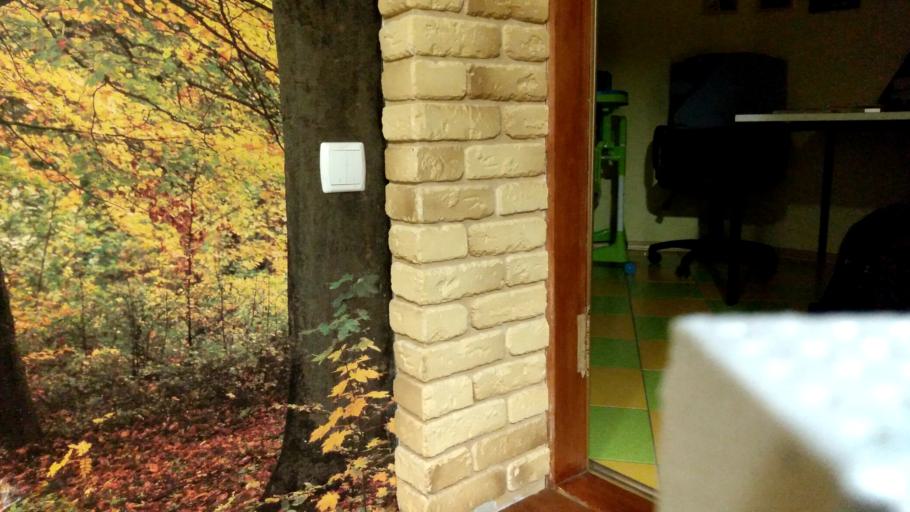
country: RU
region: Arkhangelskaya
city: Kargopol'
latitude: 61.4640
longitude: 37.7932
